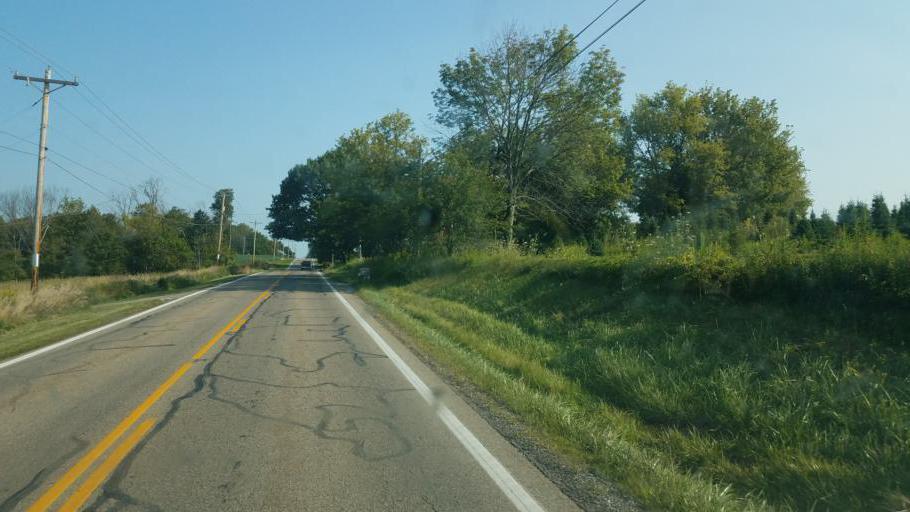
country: US
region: Ohio
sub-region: Richland County
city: Lexington
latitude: 40.6539
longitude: -82.6637
